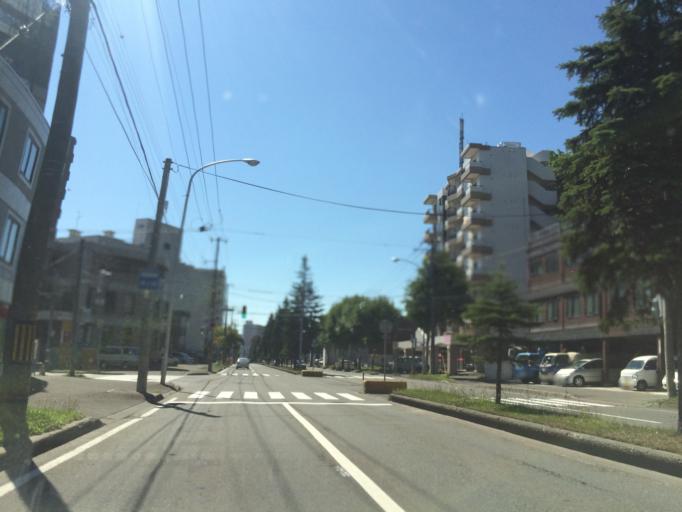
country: JP
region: Hokkaido
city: Sapporo
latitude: 43.0499
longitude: 141.3188
